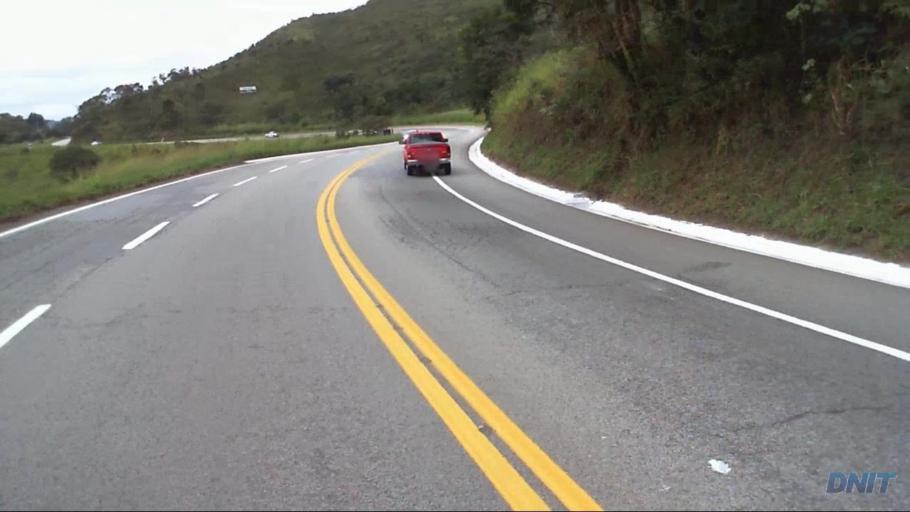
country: BR
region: Minas Gerais
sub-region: Caete
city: Caete
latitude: -19.7874
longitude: -43.6920
